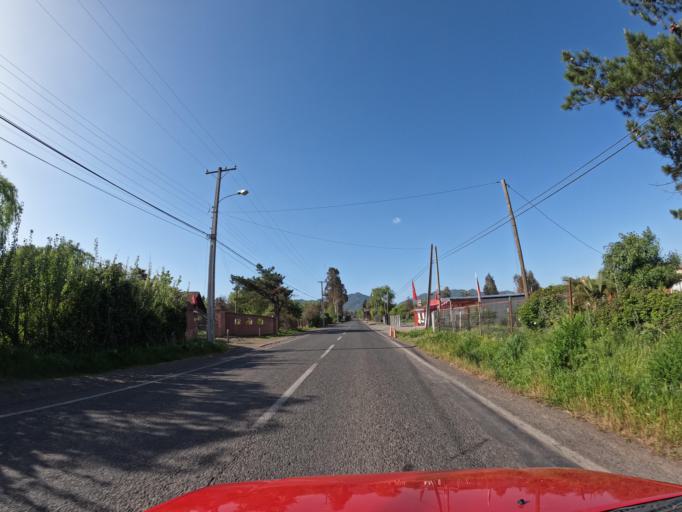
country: CL
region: Maule
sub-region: Provincia de Curico
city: Rauco
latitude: -34.8739
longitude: -71.2668
